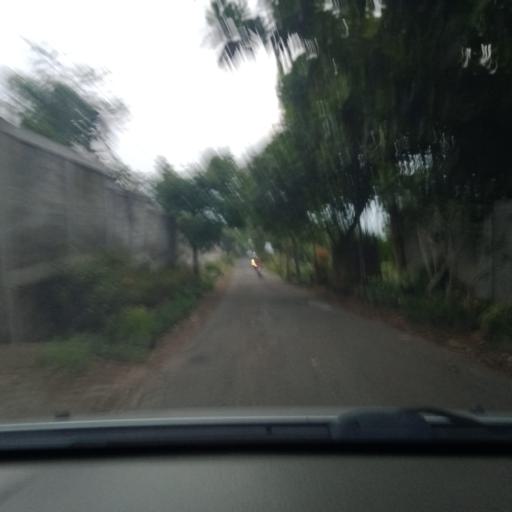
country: ID
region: West Java
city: Lembang
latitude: -6.8240
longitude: 107.5858
